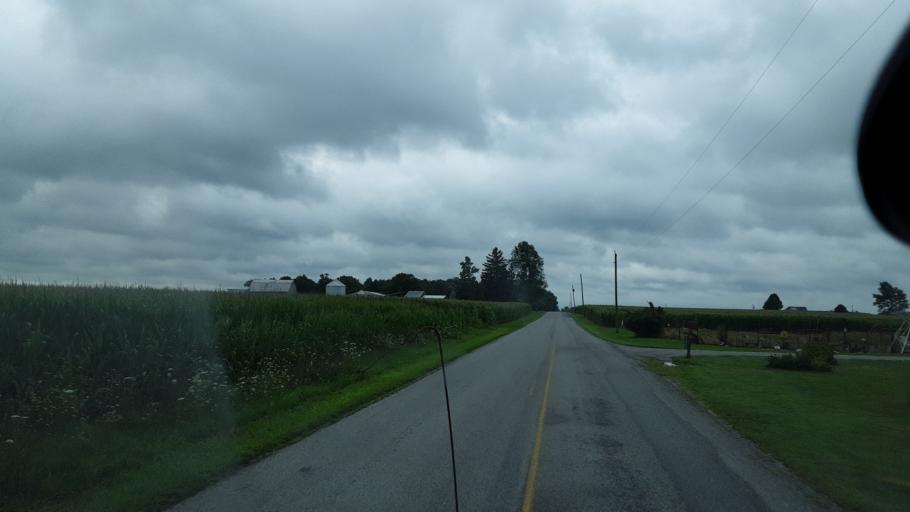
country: US
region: Indiana
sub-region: Wells County
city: Ossian
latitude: 40.9135
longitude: -85.1095
